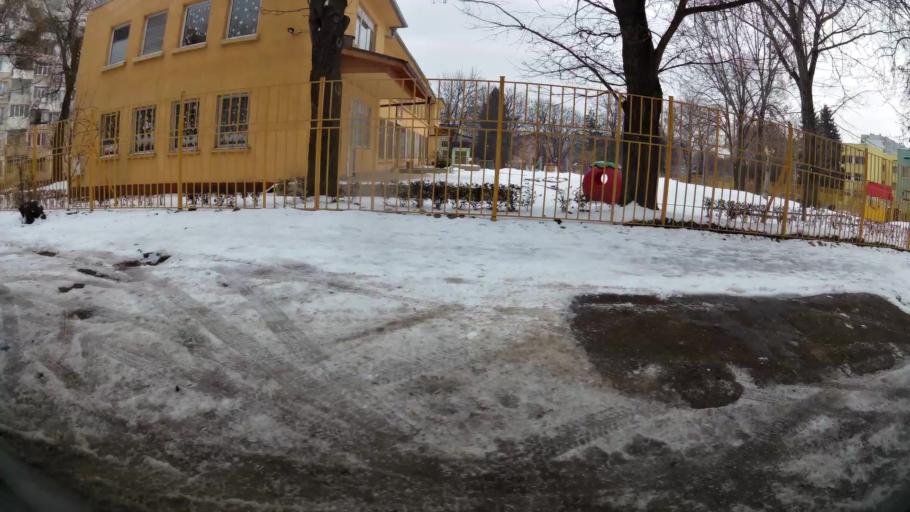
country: BG
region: Sofia-Capital
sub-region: Stolichna Obshtina
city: Sofia
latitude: 42.7146
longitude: 23.2999
